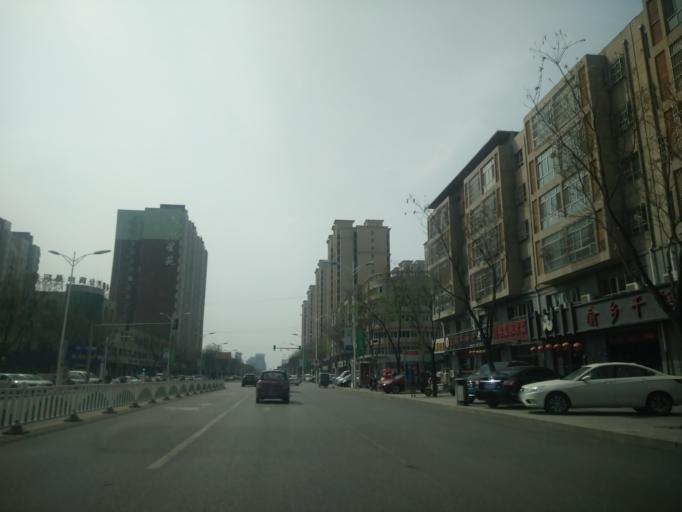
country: CN
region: Beijing
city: Xiji
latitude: 39.7639
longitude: 117.0103
